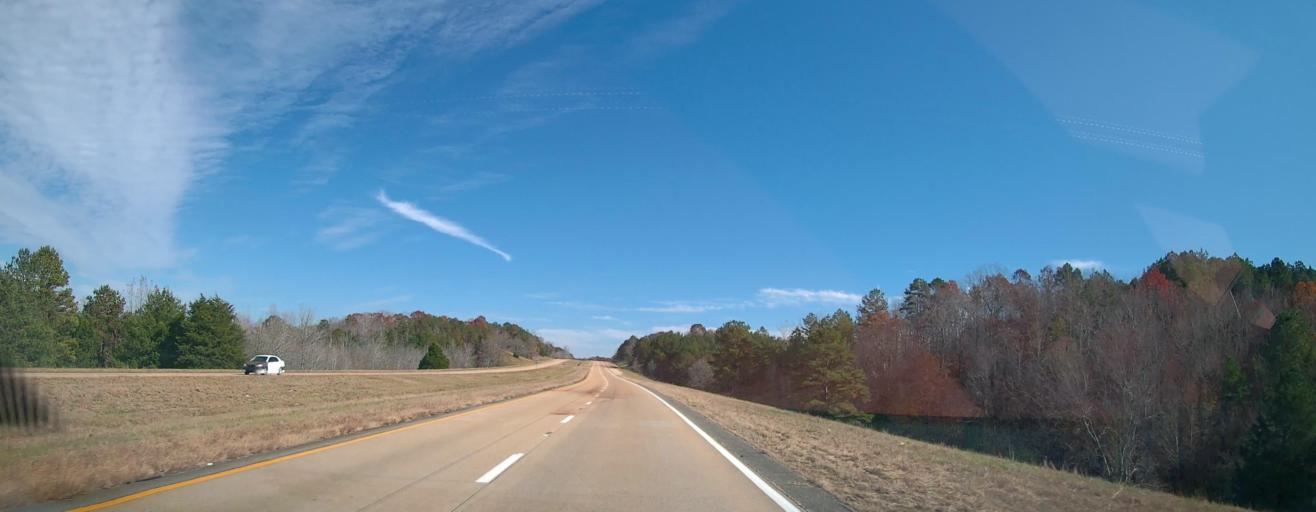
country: US
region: Mississippi
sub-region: Tishomingo County
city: Iuka
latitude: 34.7688
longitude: -88.1332
